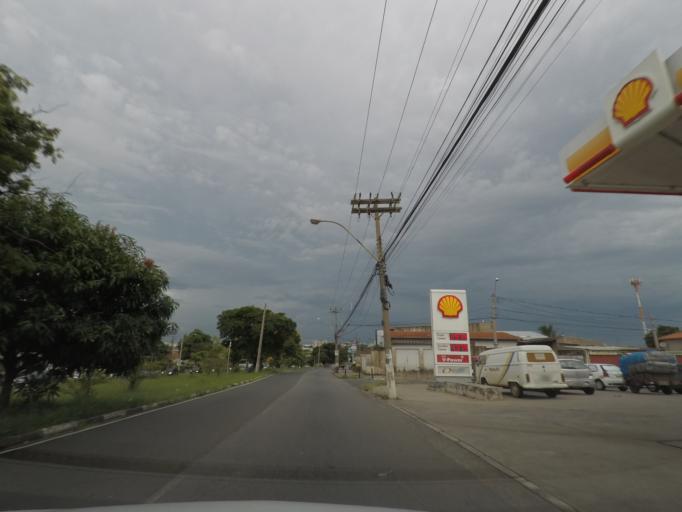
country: BR
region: Sao Paulo
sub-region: Campinas
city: Campinas
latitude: -22.9302
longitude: -47.0991
